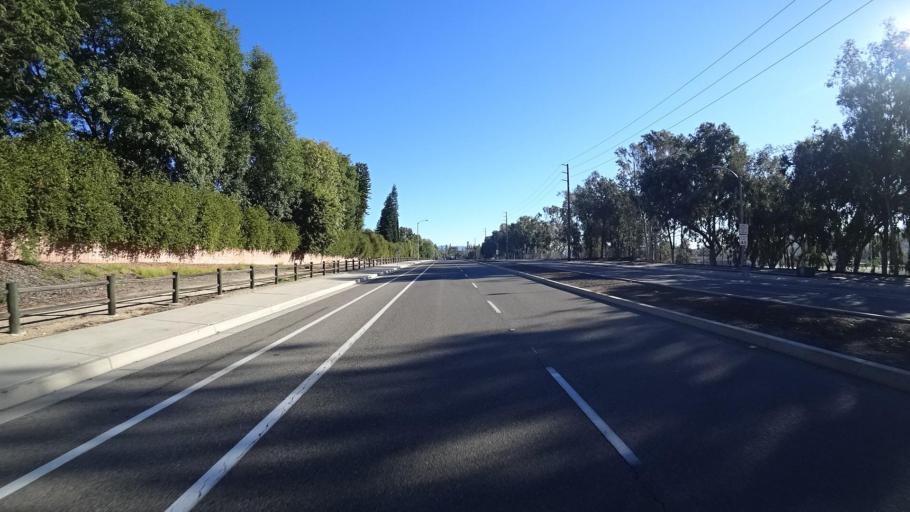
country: US
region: California
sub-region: Orange County
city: Laguna Hills
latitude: 33.5933
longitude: -117.7066
